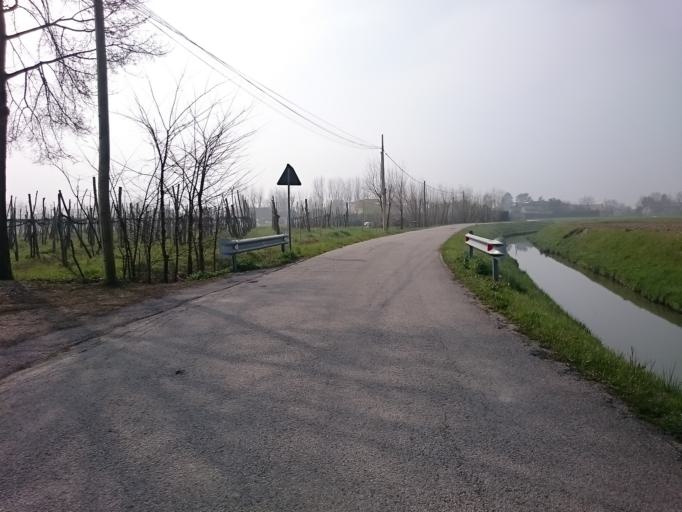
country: IT
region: Veneto
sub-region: Provincia di Padova
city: Due Carrare
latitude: 45.2864
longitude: 11.8331
